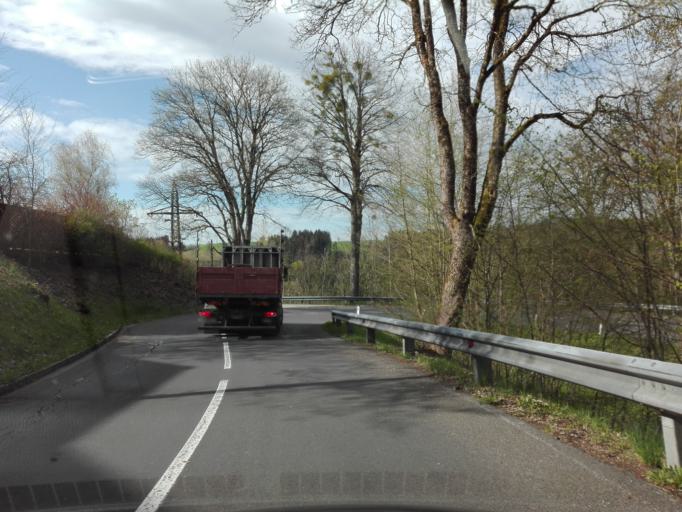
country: AT
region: Upper Austria
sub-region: Politischer Bezirk Rohrbach
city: Kleinzell im Muehlkreis
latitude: 48.4865
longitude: 14.0043
